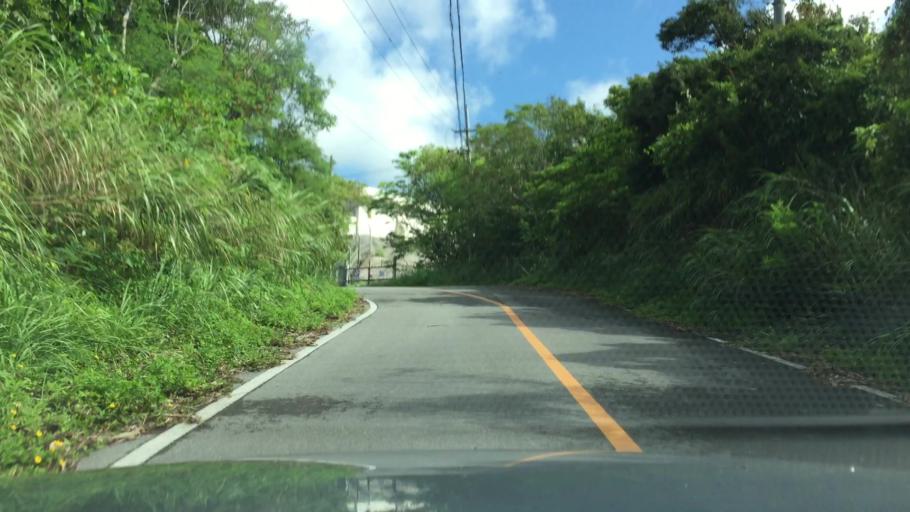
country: JP
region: Okinawa
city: Ishigaki
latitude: 24.3796
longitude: 124.1651
